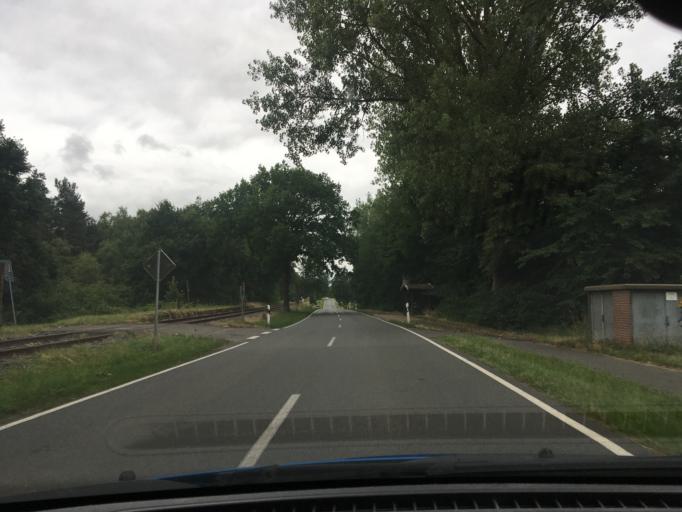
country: DE
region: Lower Saxony
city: Toppenstedt
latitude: 53.2756
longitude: 10.1247
